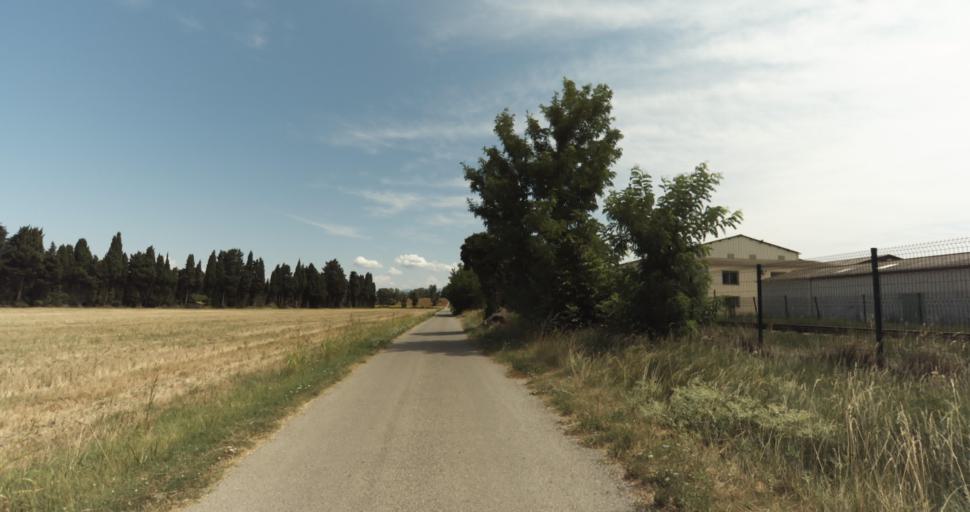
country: FR
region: Provence-Alpes-Cote d'Azur
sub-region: Departement du Vaucluse
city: Althen-des-Paluds
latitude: 44.0266
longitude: 4.9638
